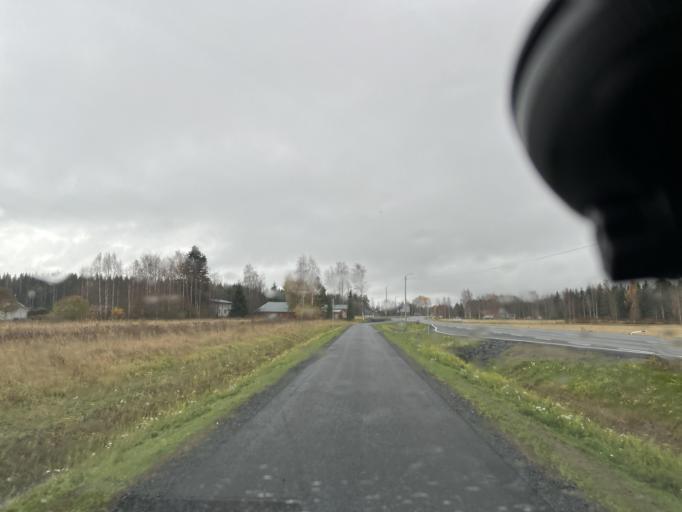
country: FI
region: Northern Ostrobothnia
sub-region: Ylivieska
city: Sievi
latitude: 63.9487
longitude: 24.5195
